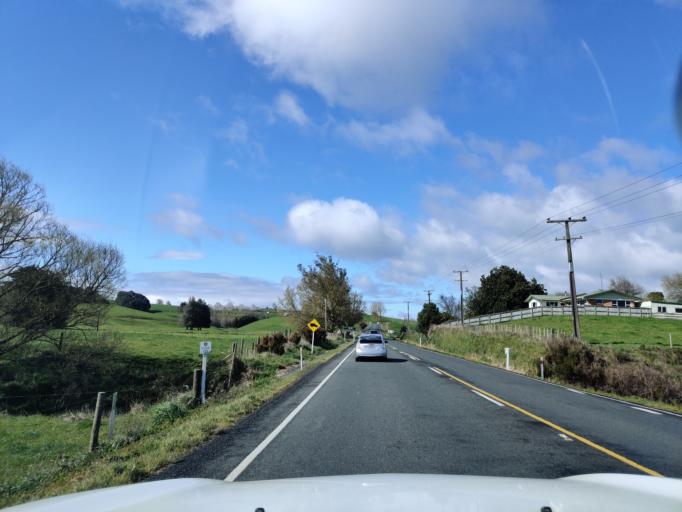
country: NZ
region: Waikato
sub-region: Otorohanga District
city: Otorohanga
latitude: -38.0884
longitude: 175.1819
